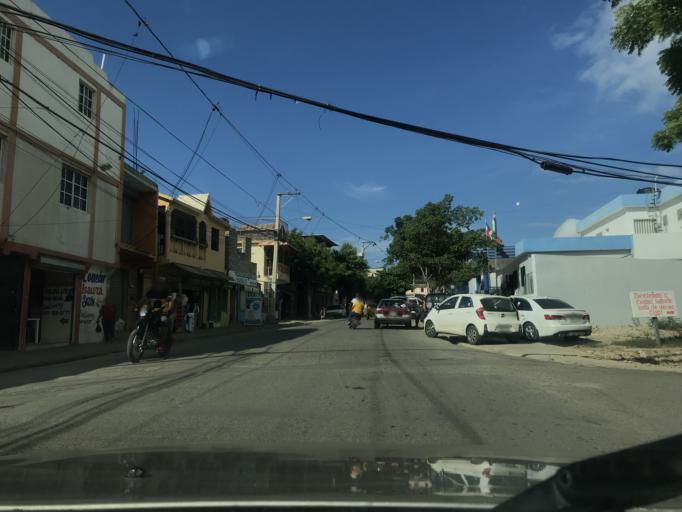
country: DO
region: Santiago
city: Palmar Arriba
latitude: 19.4849
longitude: -70.7480
